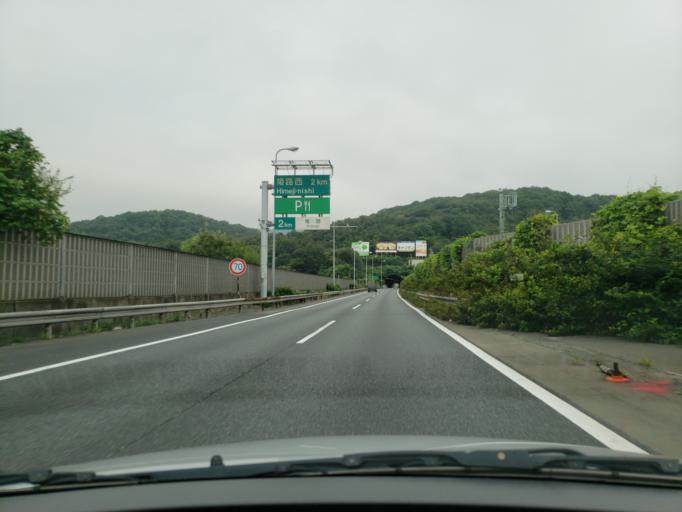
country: JP
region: Hyogo
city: Himeji
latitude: 34.8180
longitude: 134.6470
